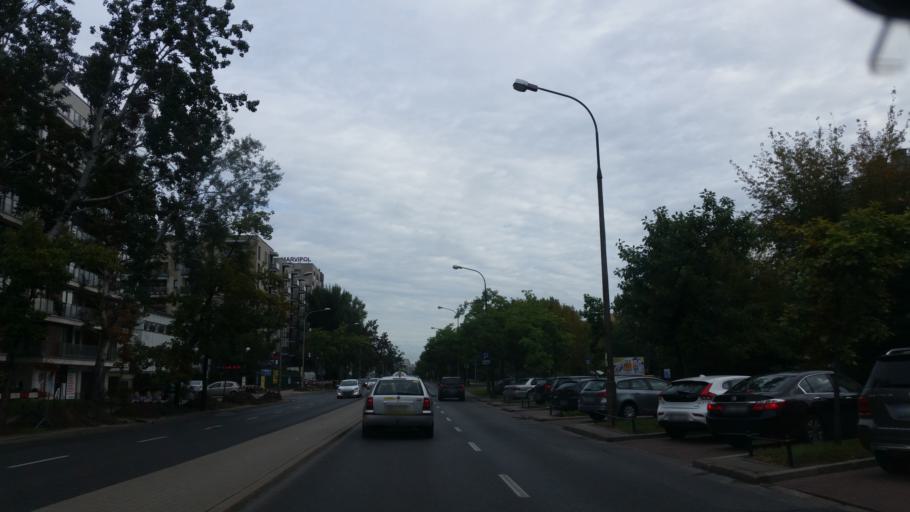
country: PL
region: Masovian Voivodeship
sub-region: Warszawa
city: Bielany
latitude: 52.2823
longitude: 20.9256
